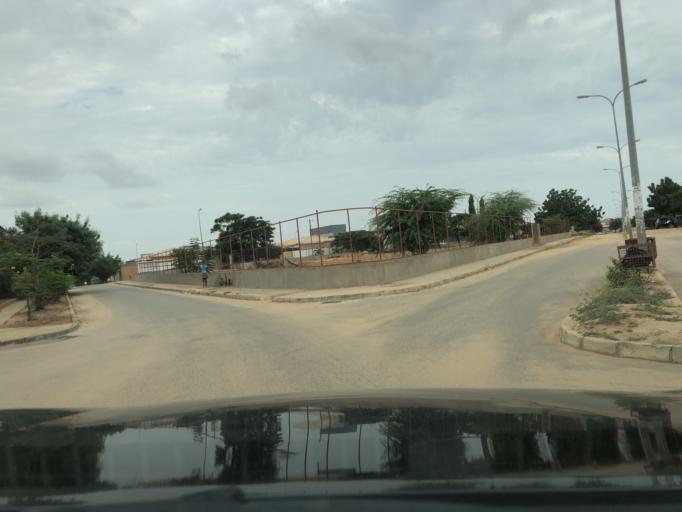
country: AO
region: Luanda
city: Luanda
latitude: -8.9350
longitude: 13.2470
